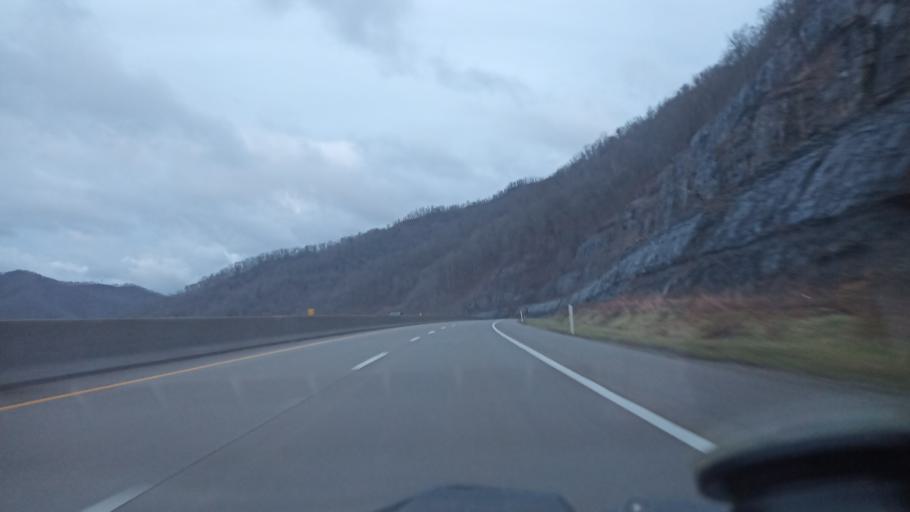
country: US
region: West Virginia
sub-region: Logan County
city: Mallory
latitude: 37.7652
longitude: -81.9188
